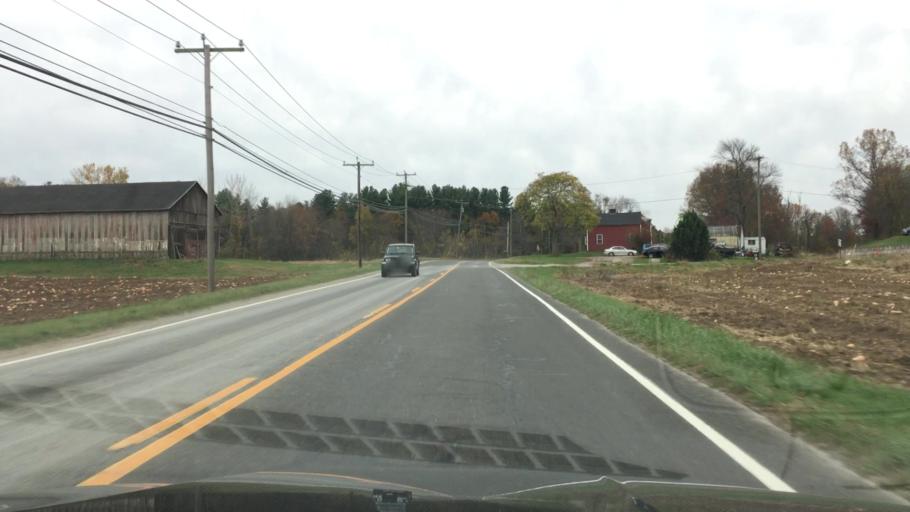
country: US
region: Connecticut
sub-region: Hartford County
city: Hazardville
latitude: 41.9741
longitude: -72.5151
